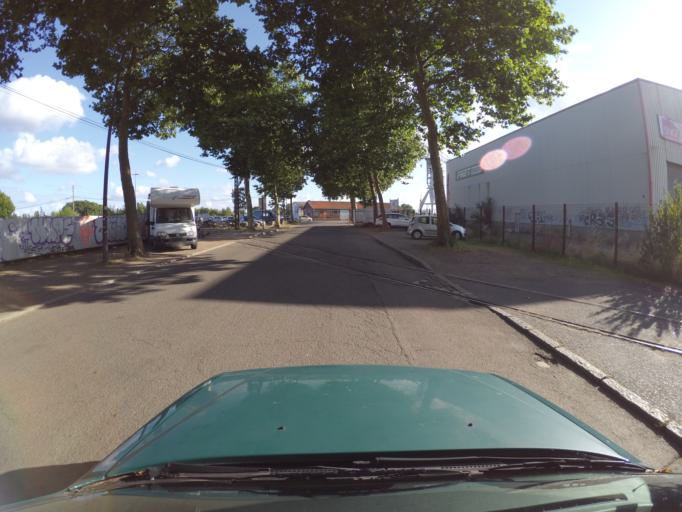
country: FR
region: Pays de la Loire
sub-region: Departement de la Loire-Atlantique
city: Nantes
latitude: 47.2005
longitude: -1.5721
